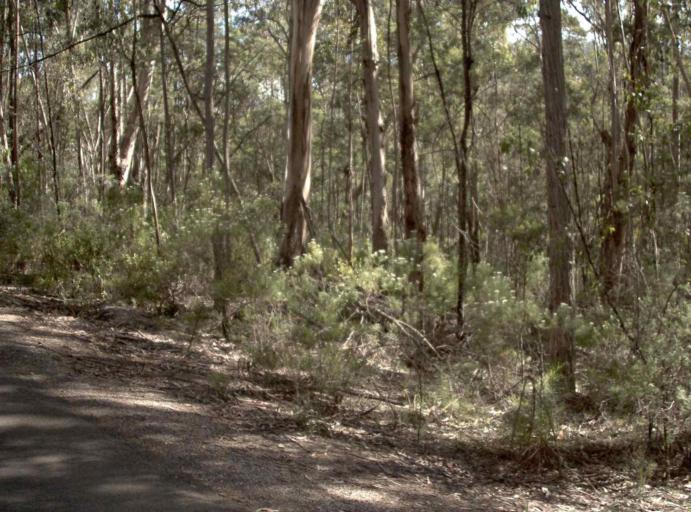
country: AU
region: Victoria
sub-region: East Gippsland
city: Lakes Entrance
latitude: -37.4329
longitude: 148.1289
